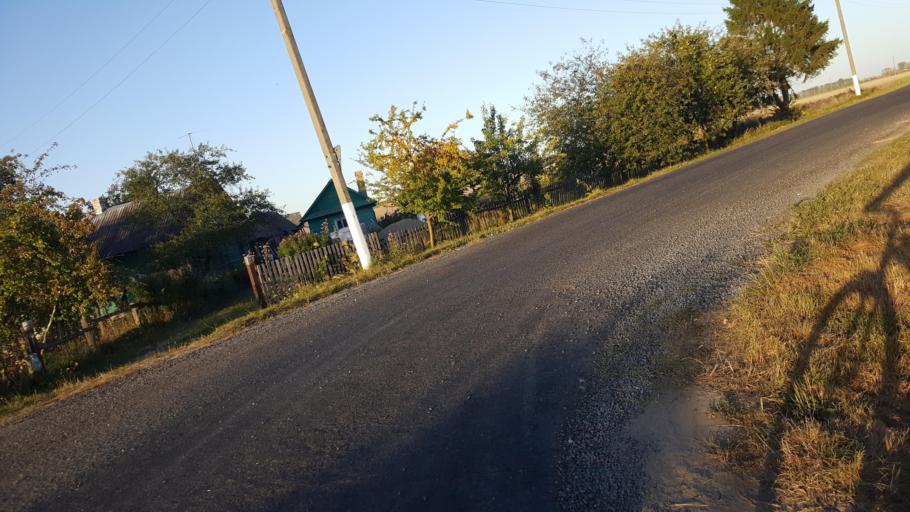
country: BY
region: Brest
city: Vysokaye
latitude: 52.2998
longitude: 23.4882
